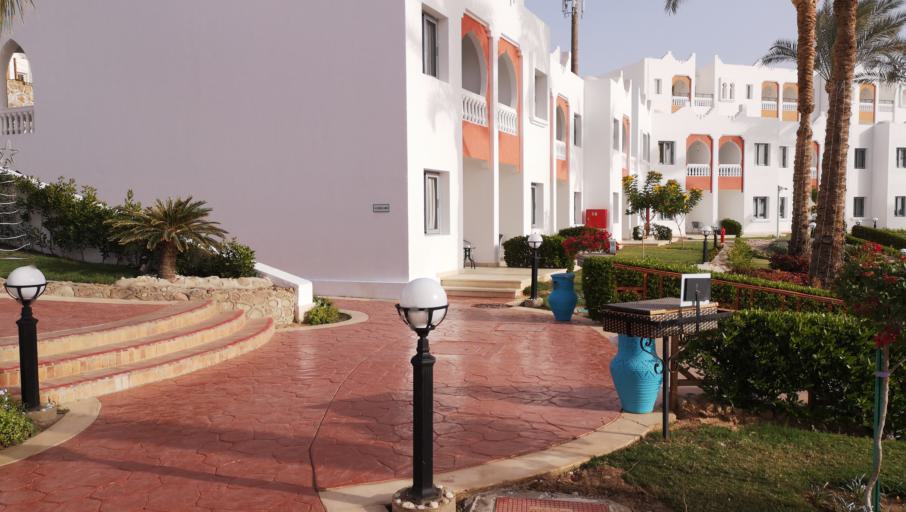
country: EG
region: South Sinai
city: Sharm el-Sheikh
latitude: 27.8642
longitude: 34.3192
